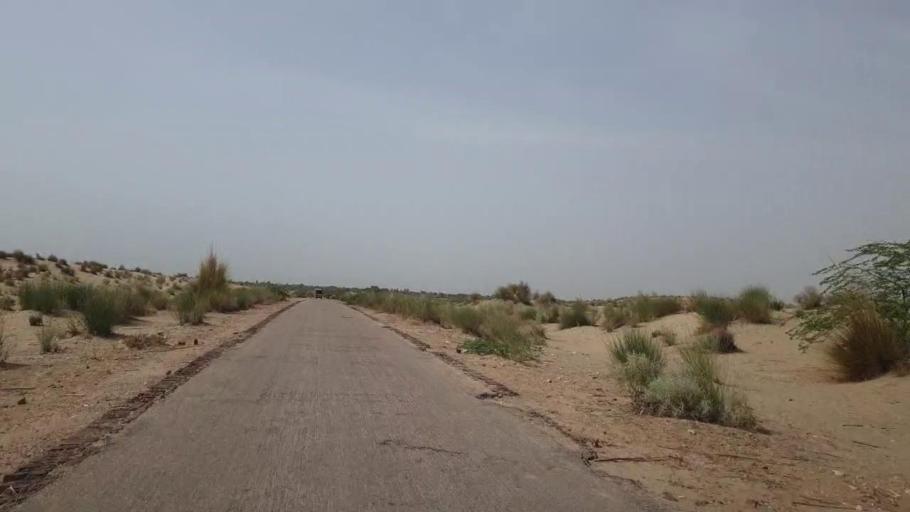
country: PK
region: Sindh
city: Bandhi
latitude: 26.5576
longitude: 68.3826
